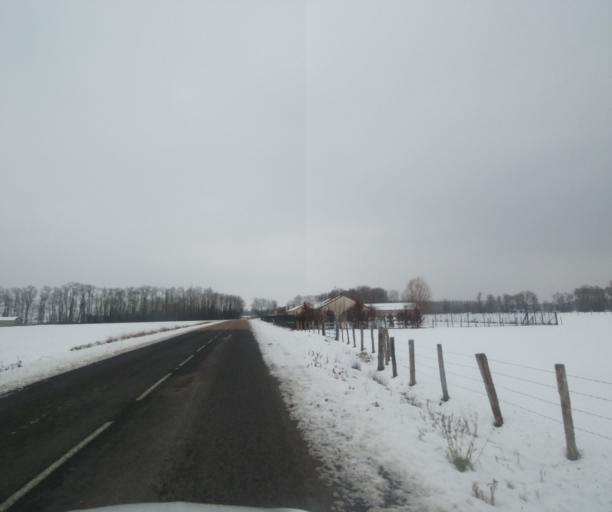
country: FR
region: Champagne-Ardenne
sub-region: Departement de la Haute-Marne
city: Villiers-en-Lieu
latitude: 48.5954
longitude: 4.8452
